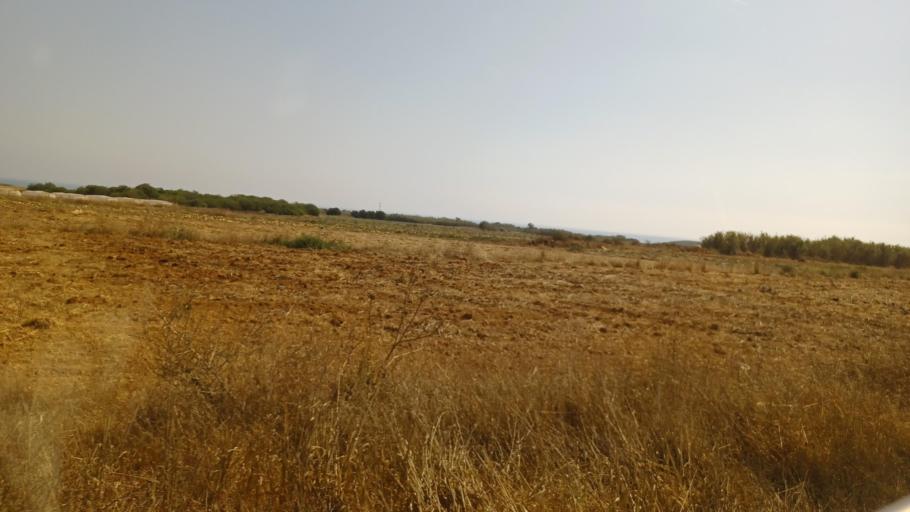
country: CY
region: Ammochostos
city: Paralimni
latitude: 35.0642
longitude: 33.9916
